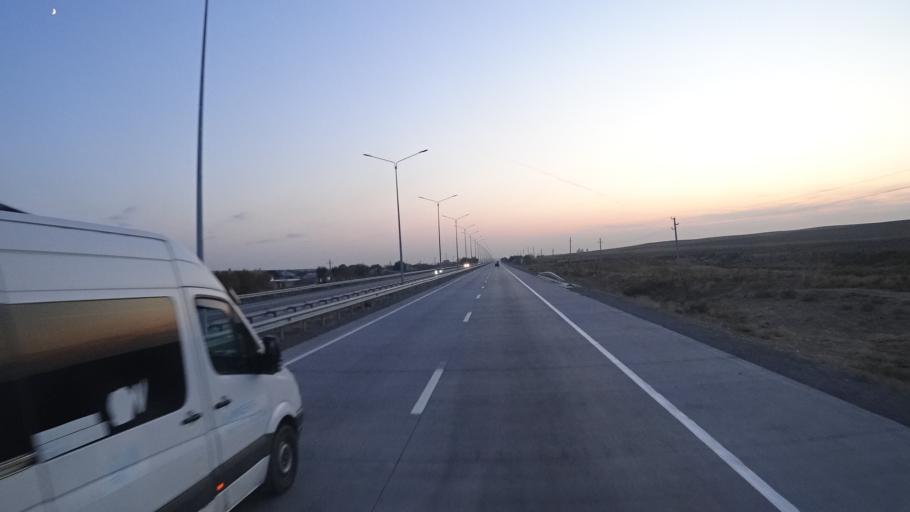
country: KZ
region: Ongtustik Qazaqstan
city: Qazyqurt
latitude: 41.8905
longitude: 69.4472
